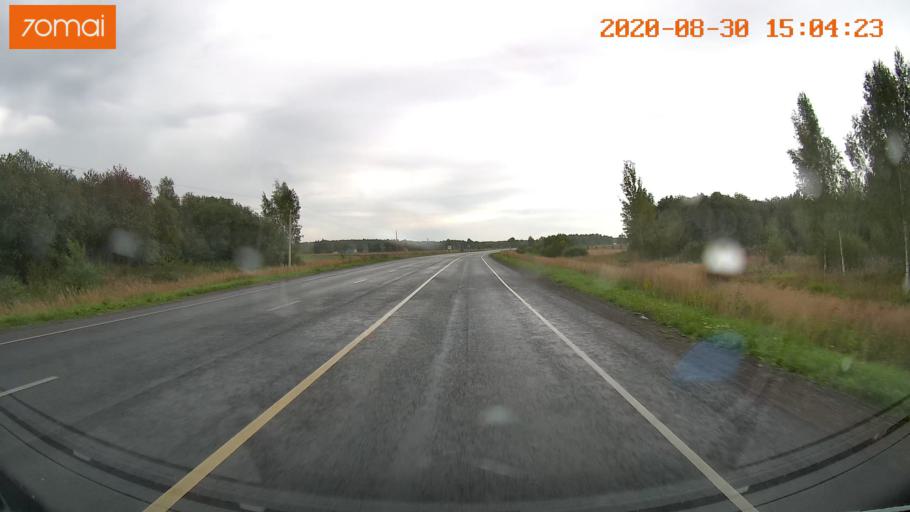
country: RU
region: Ivanovo
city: Staraya Vichuga
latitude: 57.2874
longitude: 41.9091
